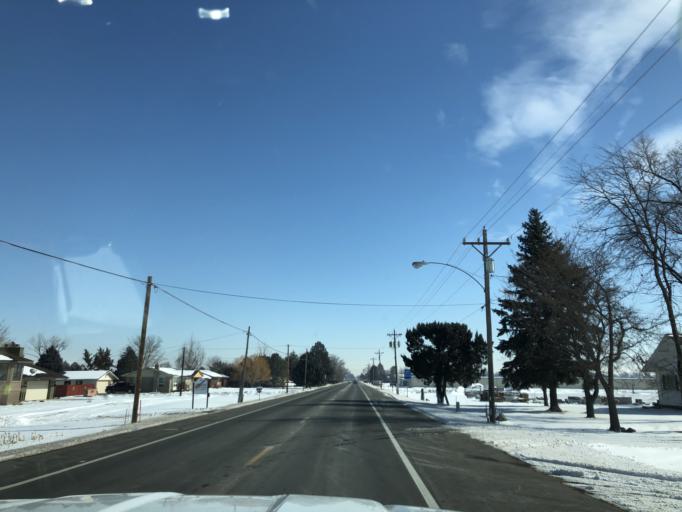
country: US
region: Colorado
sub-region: Morgan County
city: Fort Morgan
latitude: 40.2540
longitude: -103.8259
